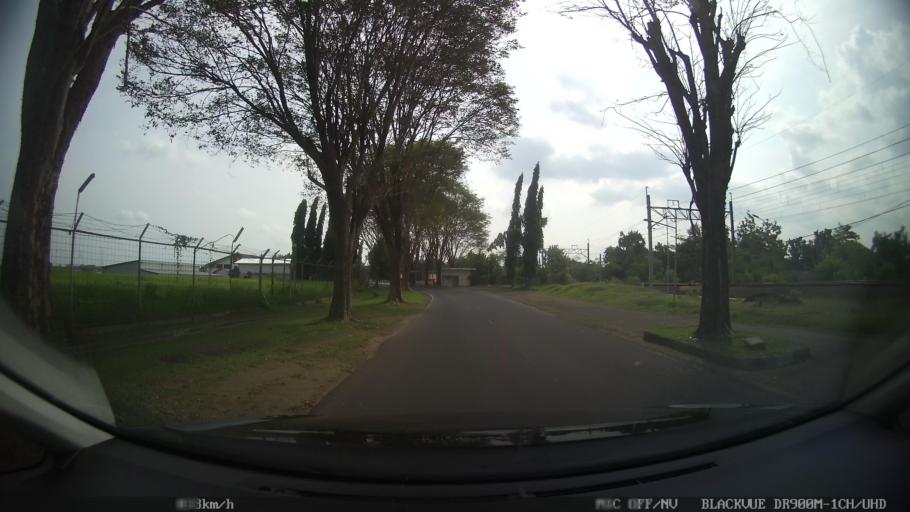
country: ID
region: Daerah Istimewa Yogyakarta
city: Depok
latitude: -7.7850
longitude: 110.4406
